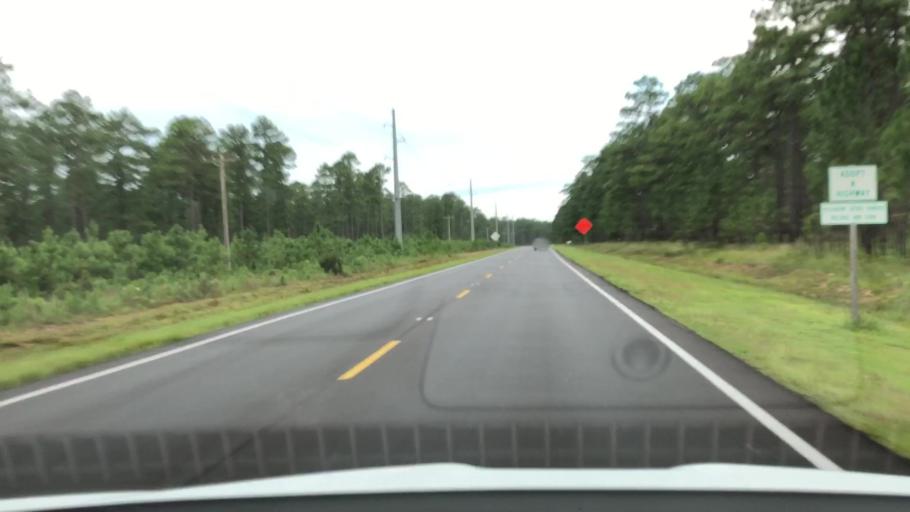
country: US
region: North Carolina
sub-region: Onslow County
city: Swansboro
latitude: 34.8130
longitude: -77.1399
